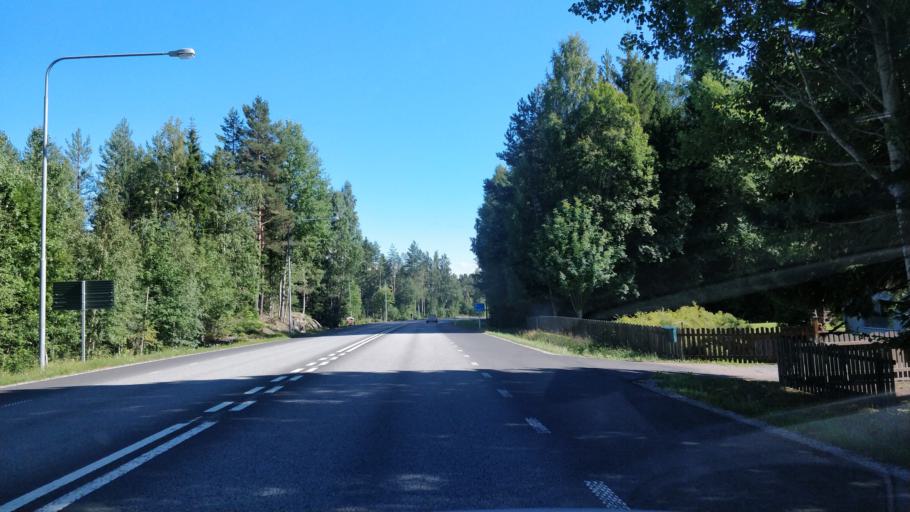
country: SE
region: Dalarna
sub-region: Faluns Kommun
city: Bjursas
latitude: 60.7288
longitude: 15.4439
